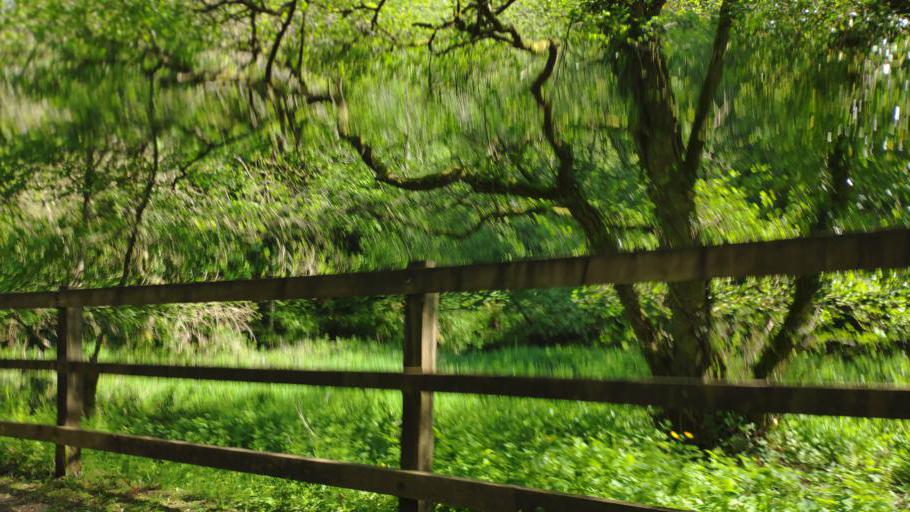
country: IE
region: Munster
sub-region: County Cork
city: Blarney
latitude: 51.9418
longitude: -8.5645
